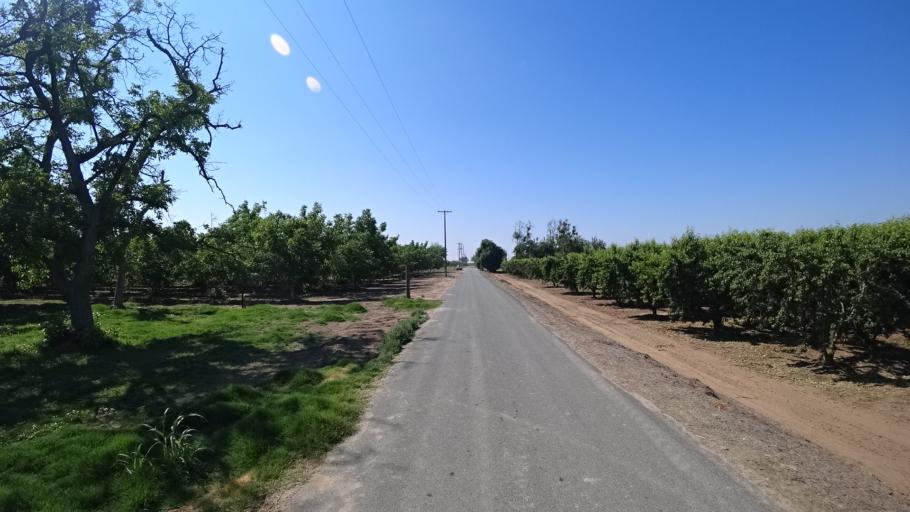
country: US
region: California
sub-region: Fresno County
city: Kingsburg
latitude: 36.4479
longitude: -119.5629
